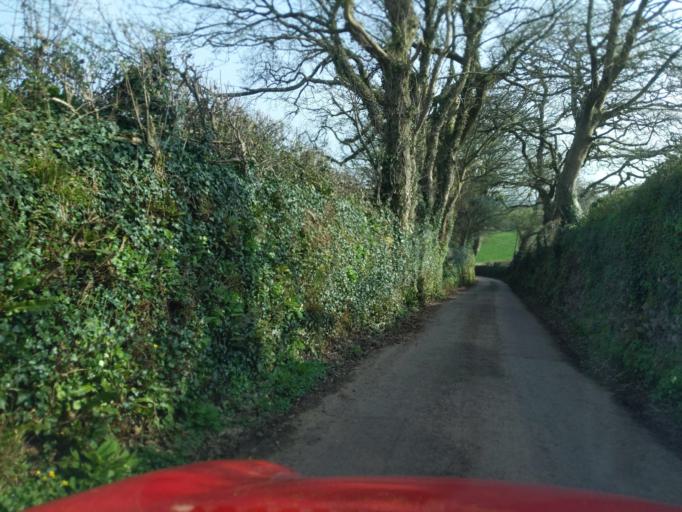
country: GB
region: England
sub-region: Devon
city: Kingsbridge
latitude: 50.2866
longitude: -3.7265
